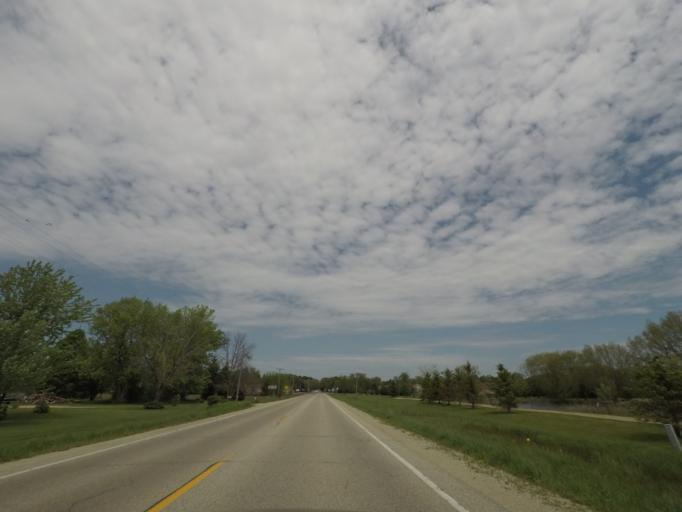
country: US
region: Wisconsin
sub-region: Rock County
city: Evansville
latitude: 42.7692
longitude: -89.2990
